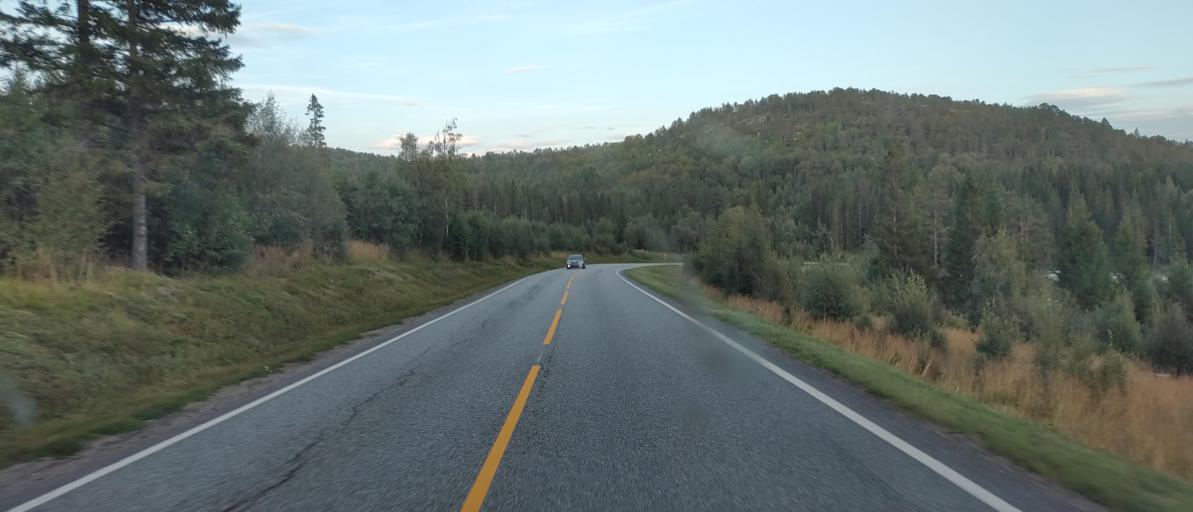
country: NO
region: Nordland
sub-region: Lodingen
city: Lodingen
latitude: 68.2106
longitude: 16.0583
